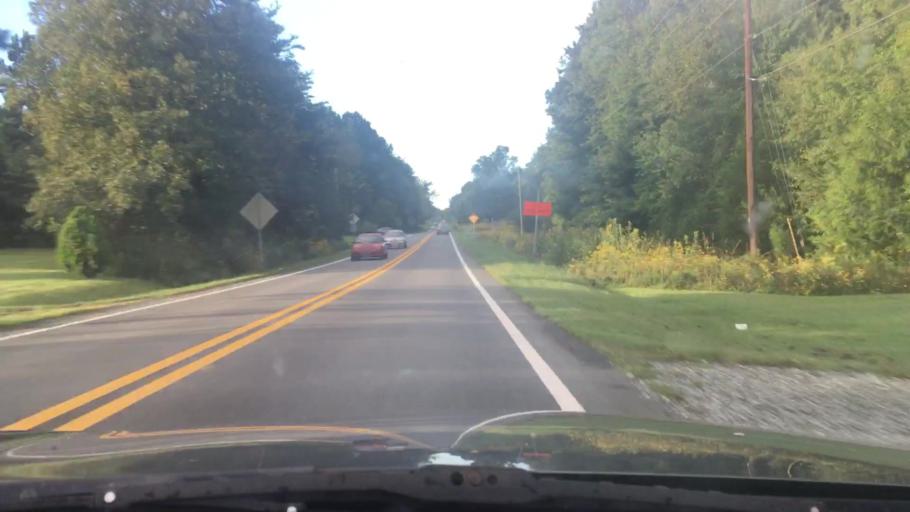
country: US
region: North Carolina
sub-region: Alamance County
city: Green Level
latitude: 36.1972
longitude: -79.3235
